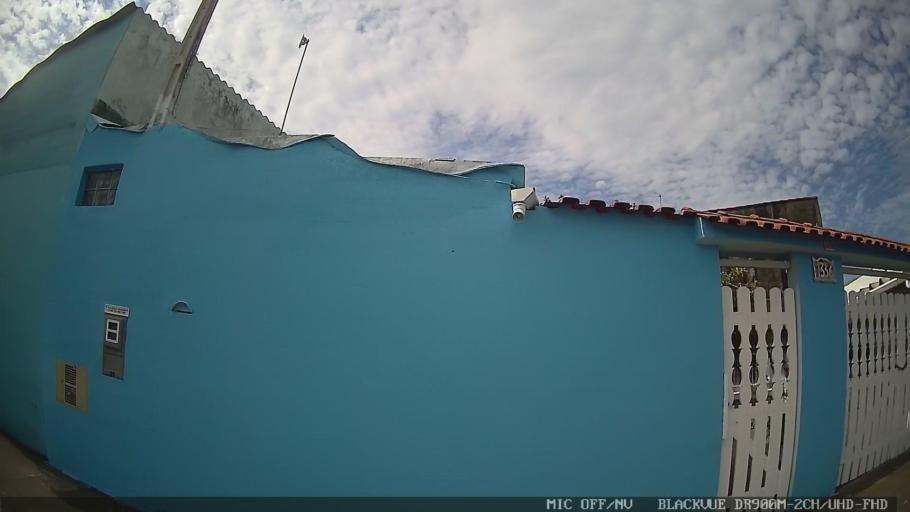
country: BR
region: Sao Paulo
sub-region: Itanhaem
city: Itanhaem
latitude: -24.1577
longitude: -46.7691
